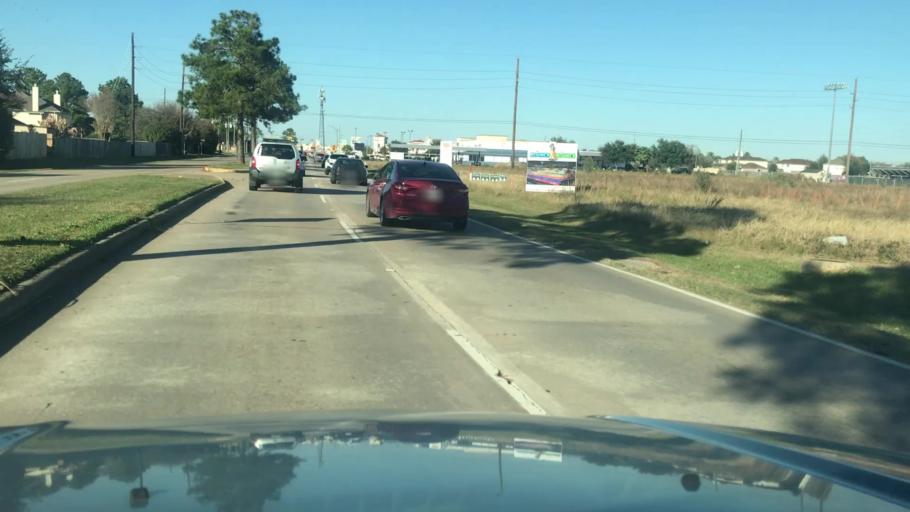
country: US
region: Texas
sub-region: Fort Bend County
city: Cinco Ranch
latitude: 29.8472
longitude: -95.7192
